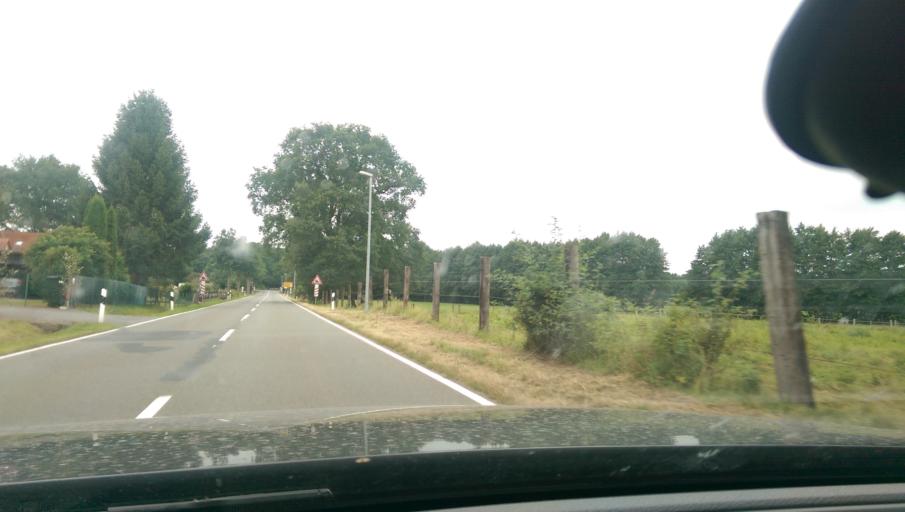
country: DE
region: Lower Saxony
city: Neustadt am Rubenberge
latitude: 52.5311
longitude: 9.4511
